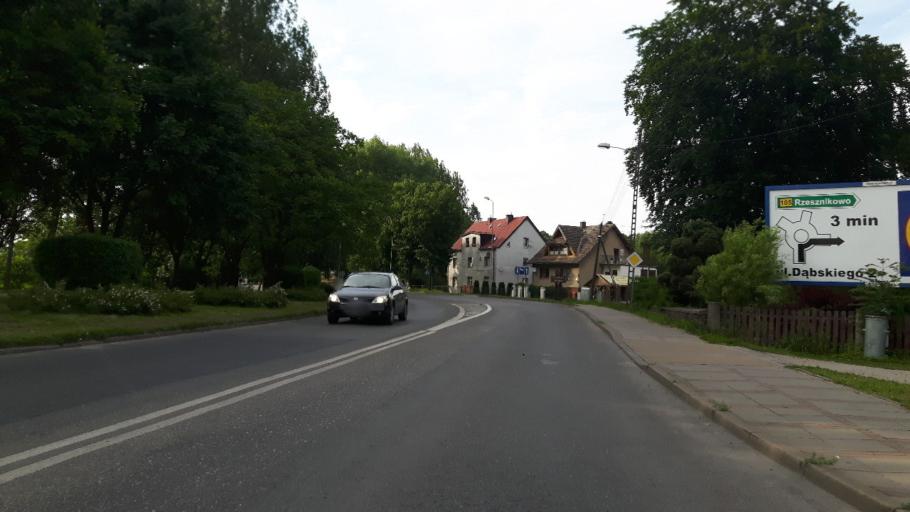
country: PL
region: West Pomeranian Voivodeship
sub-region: Powiat gryficki
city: Gryfice
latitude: 53.9091
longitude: 15.2004
